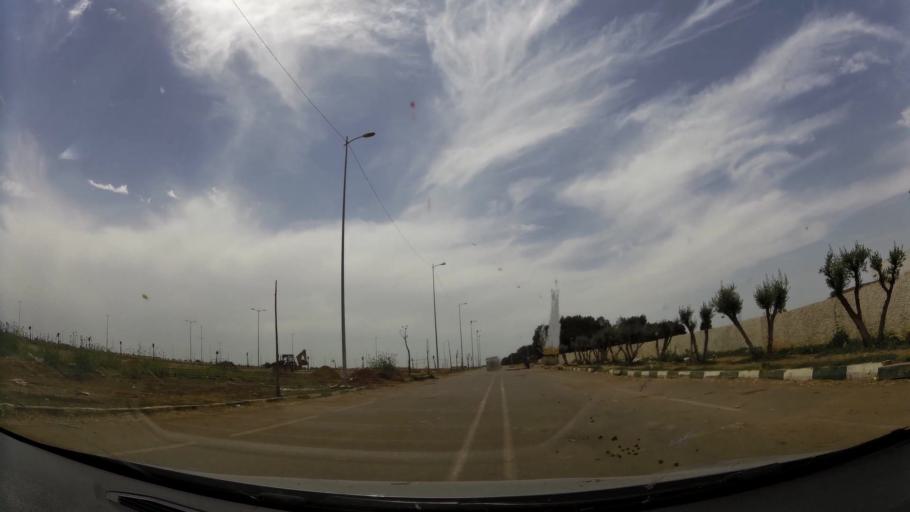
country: MA
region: Rabat-Sale-Zemmour-Zaer
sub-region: Khemisset
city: Khemisset
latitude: 33.8200
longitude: -6.0901
